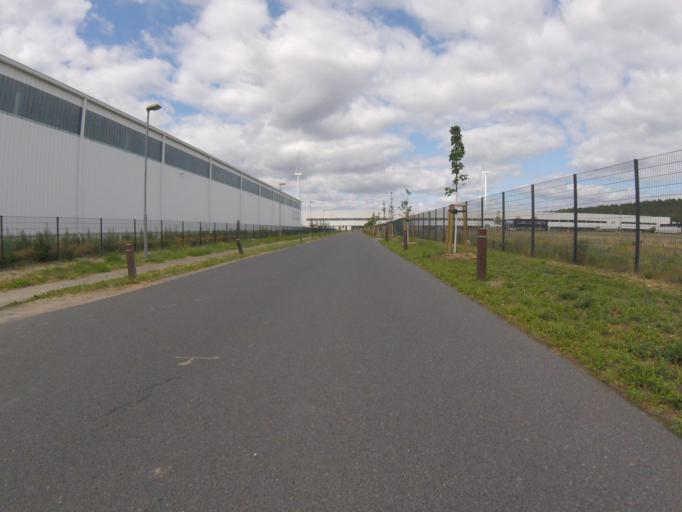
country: DE
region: Brandenburg
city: Wildau
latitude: 52.3201
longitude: 13.6740
